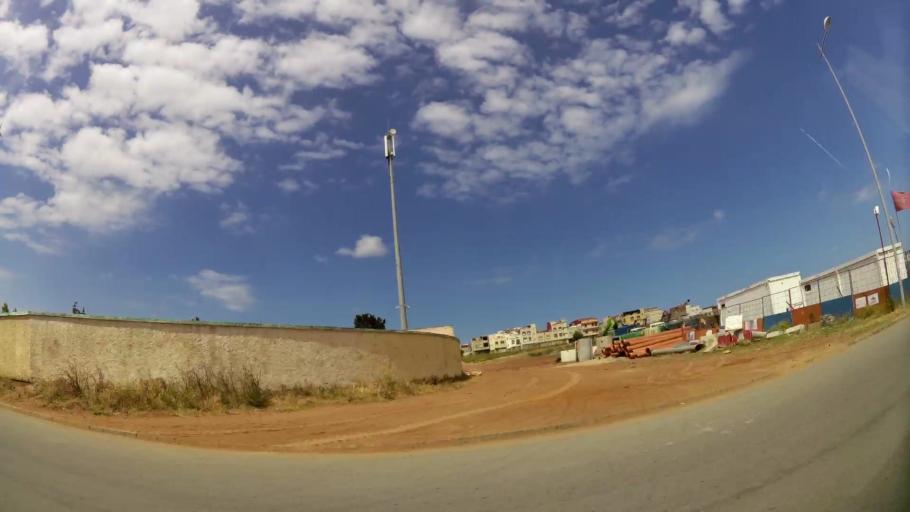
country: MA
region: Gharb-Chrarda-Beni Hssen
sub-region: Kenitra Province
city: Kenitra
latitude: 34.2449
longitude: -6.6076
